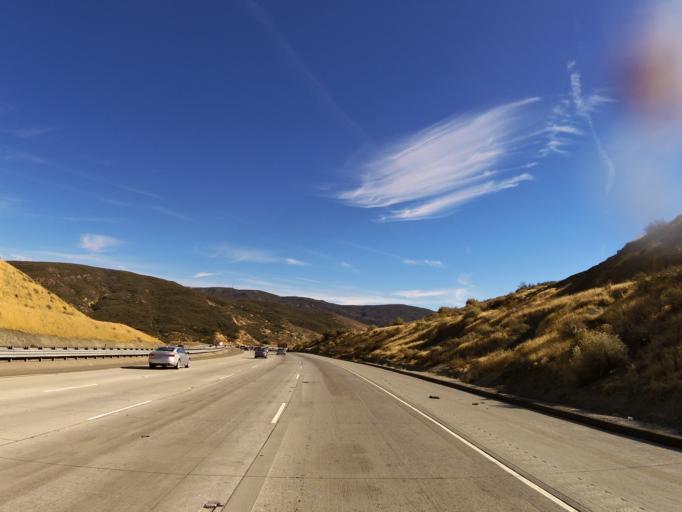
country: US
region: California
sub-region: Kern County
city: Lebec
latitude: 34.6743
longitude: -118.7749
